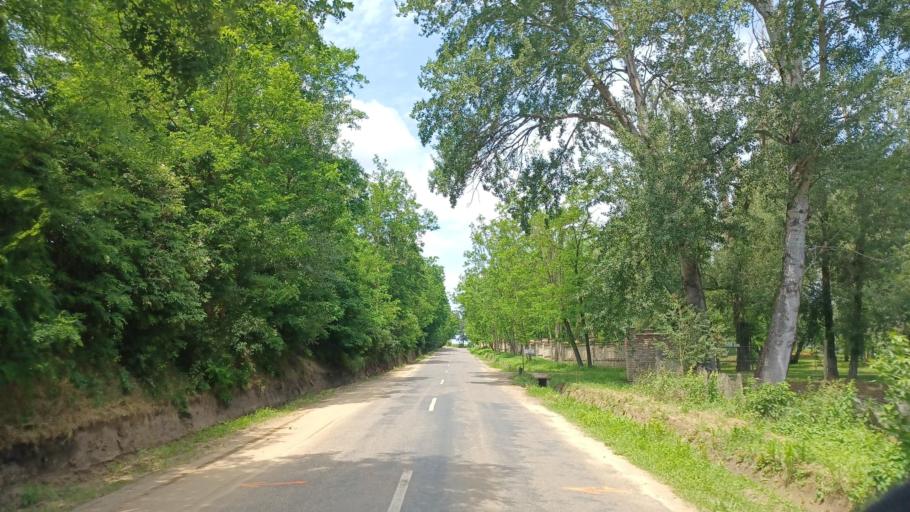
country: HU
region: Tolna
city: Simontornya
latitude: 46.6969
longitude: 18.5176
